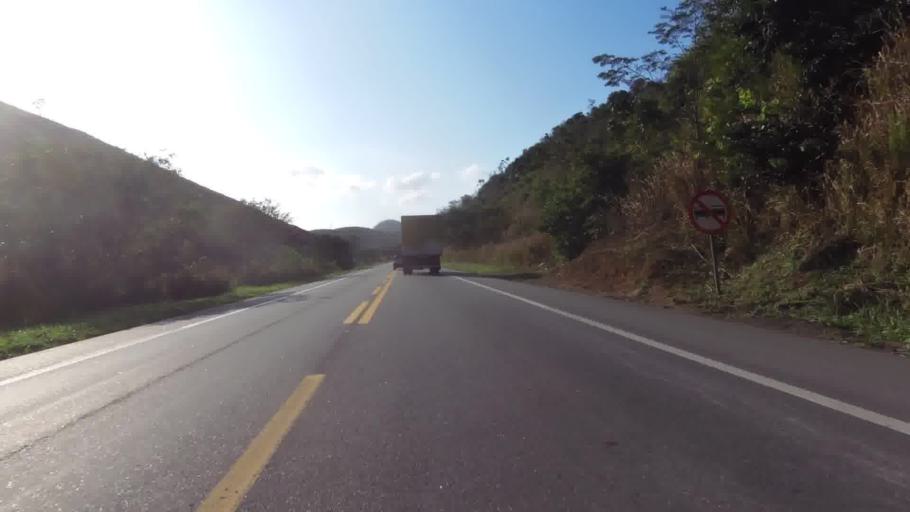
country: BR
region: Espirito Santo
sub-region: Mimoso Do Sul
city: Mimoso do Sul
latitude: -21.1819
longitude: -41.2959
